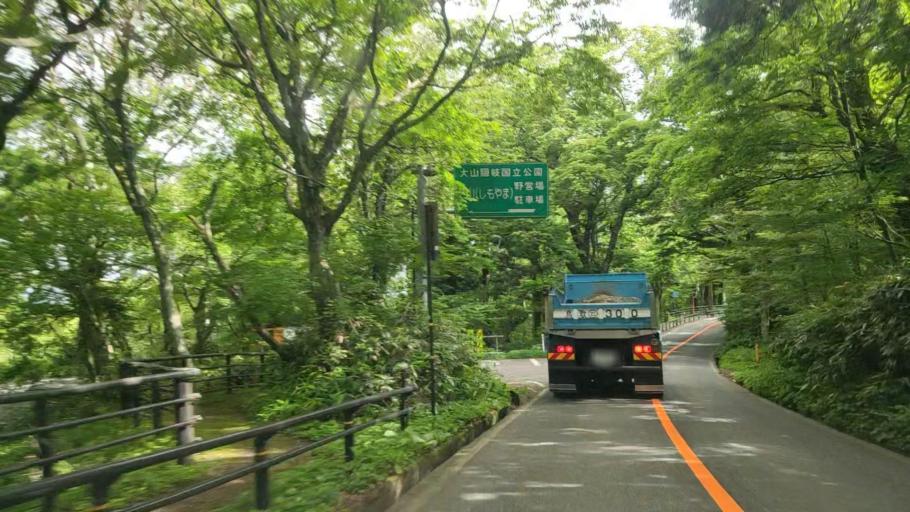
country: JP
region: Tottori
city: Yonago
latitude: 35.3904
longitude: 133.5281
